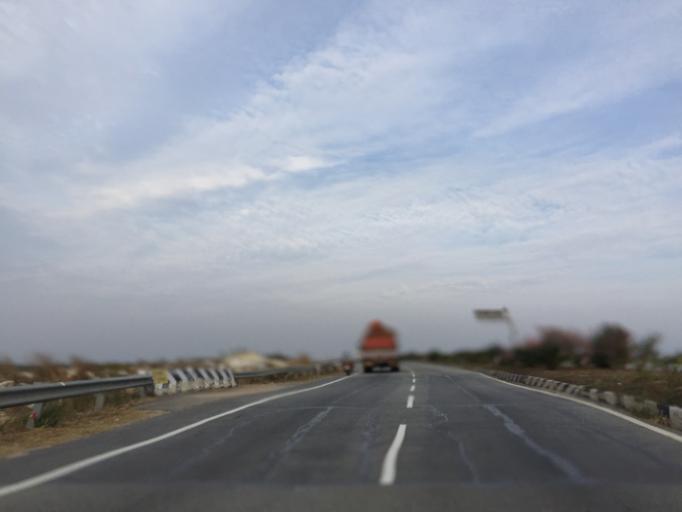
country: IN
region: Karnataka
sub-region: Kolar
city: Mulbagal
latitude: 13.1500
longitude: 78.2988
